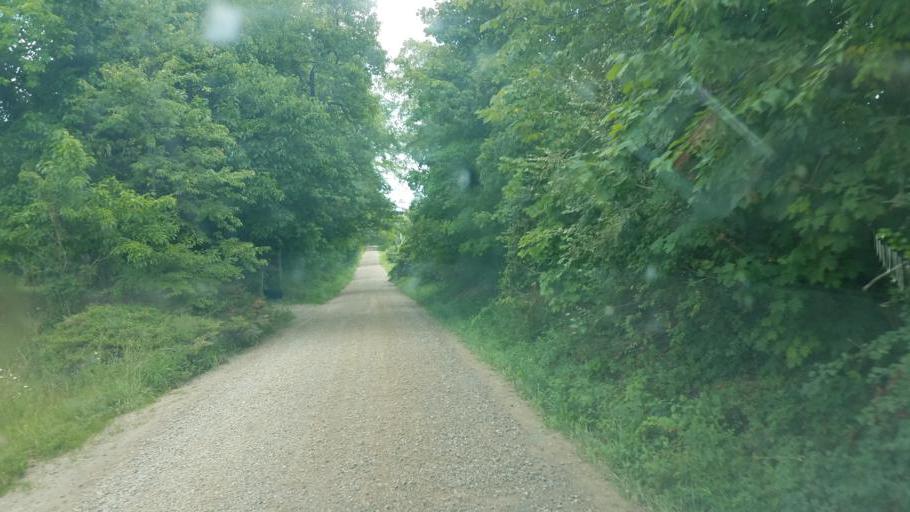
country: US
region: Ohio
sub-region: Knox County
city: Centerburg
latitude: 40.3835
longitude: -82.6148
